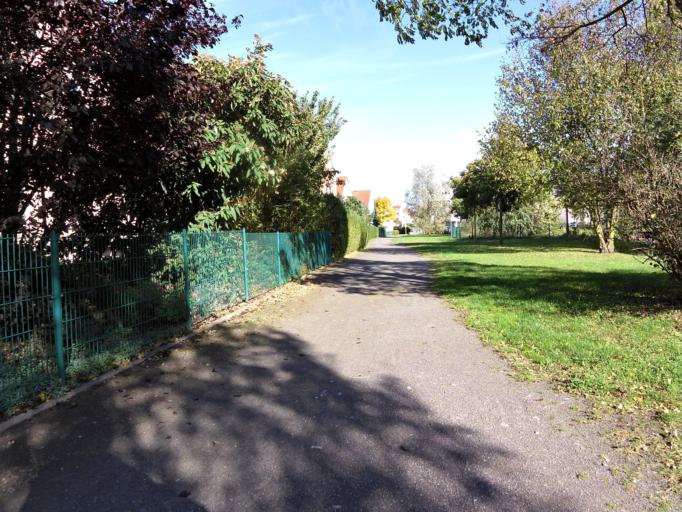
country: DE
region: Saxony
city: Grossposna
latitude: 51.3012
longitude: 12.4412
